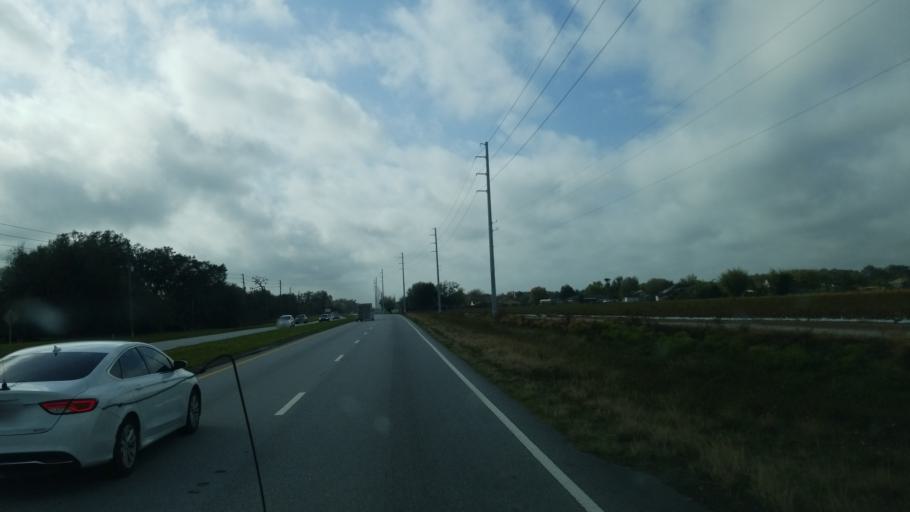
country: US
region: Florida
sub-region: Polk County
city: Winston
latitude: 27.9802
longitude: -82.0560
